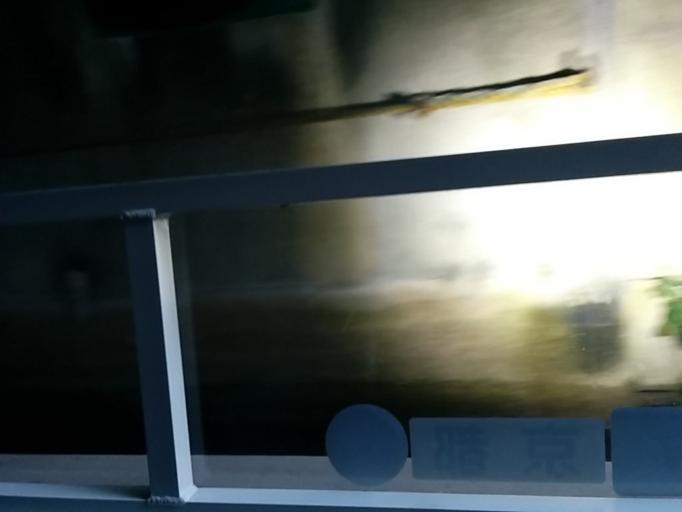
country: JP
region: Kyoto
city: Kyoto
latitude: 35.0004
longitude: 135.7984
